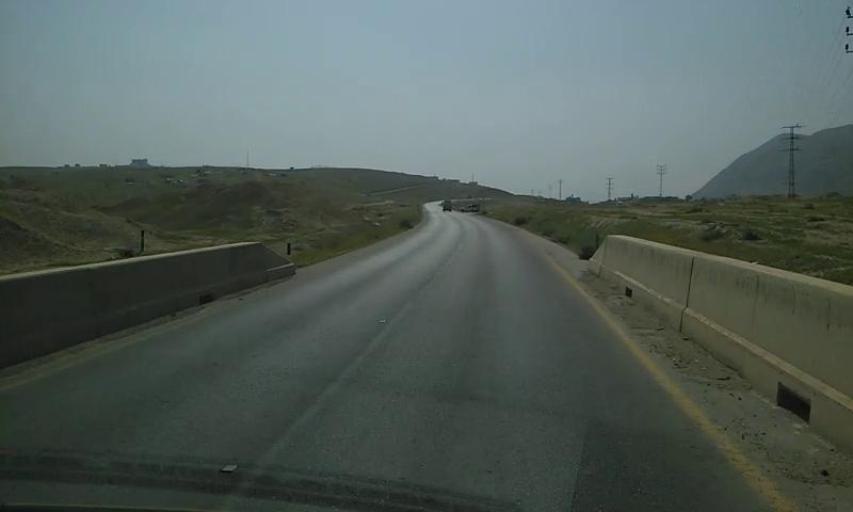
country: PS
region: West Bank
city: An Nuway`imah
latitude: 31.9017
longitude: 35.4261
